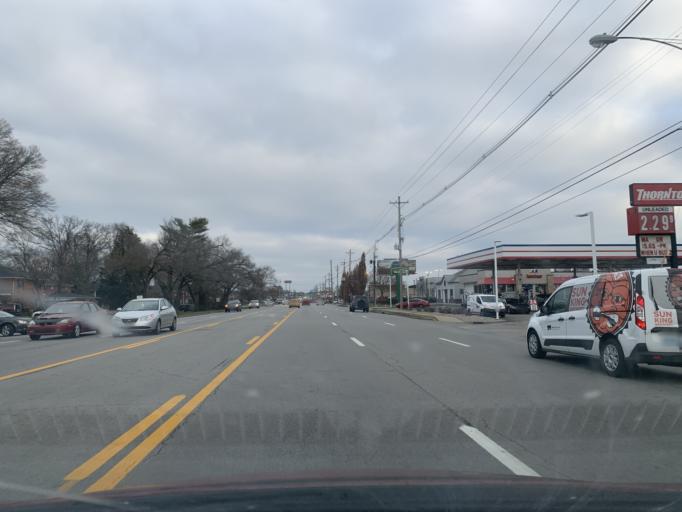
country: US
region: Kentucky
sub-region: Jefferson County
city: Beechwood Village
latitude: 38.2511
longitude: -85.6340
